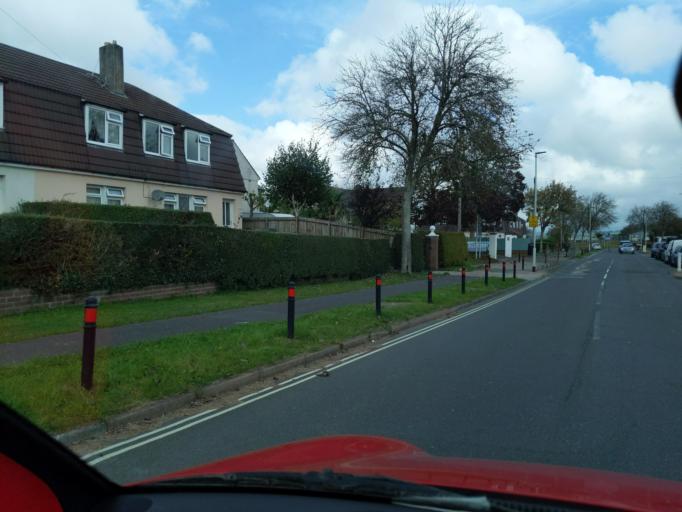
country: GB
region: England
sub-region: Cornwall
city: Torpoint
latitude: 50.4163
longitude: -4.1722
